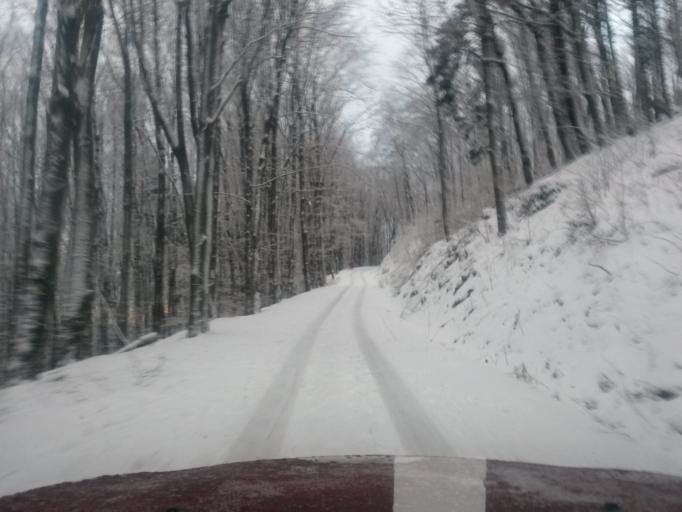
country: SK
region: Kosicky
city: Kosice
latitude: 48.7639
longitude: 21.1309
